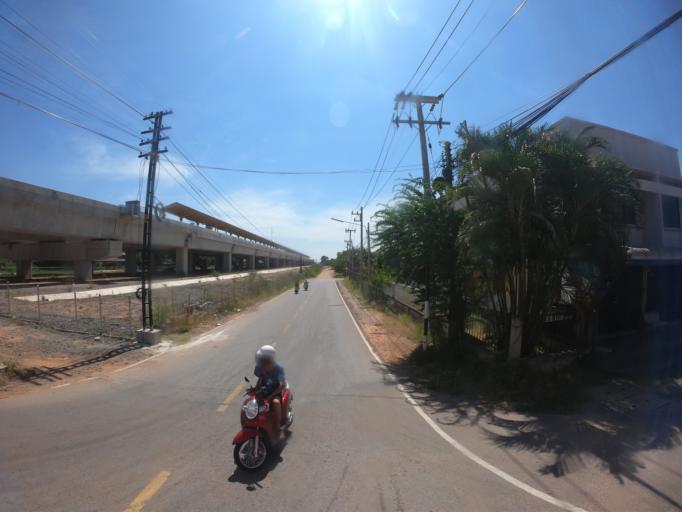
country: TH
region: Khon Kaen
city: Ban Phai
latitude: 16.0624
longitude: 102.7258
